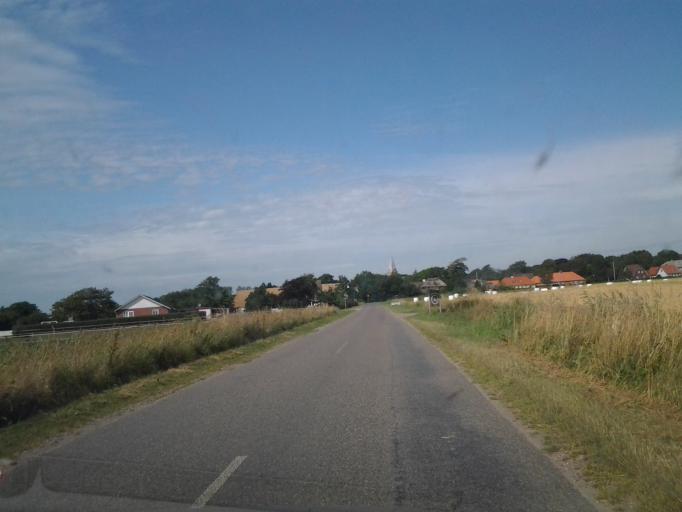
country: DE
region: Schleswig-Holstein
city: Aventoft
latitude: 54.9348
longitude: 8.7994
